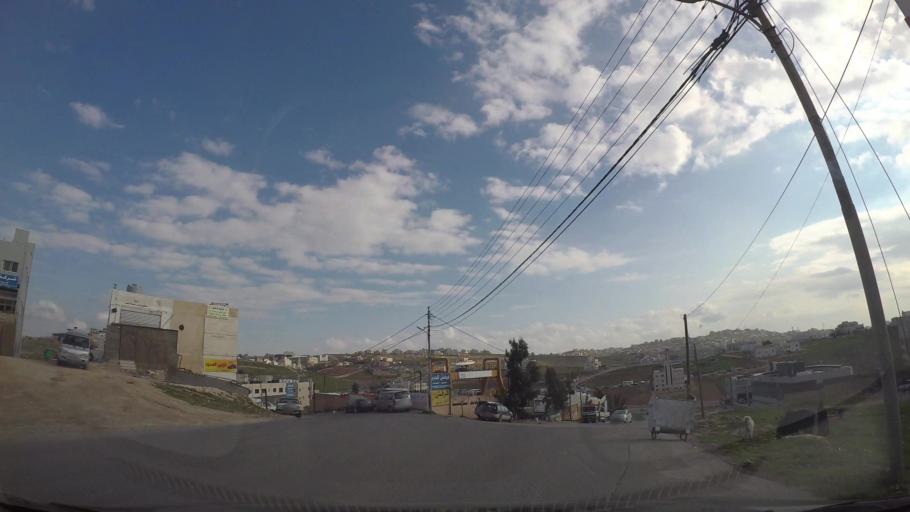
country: JO
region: Amman
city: Wadi as Sir
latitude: 31.9363
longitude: 35.8454
